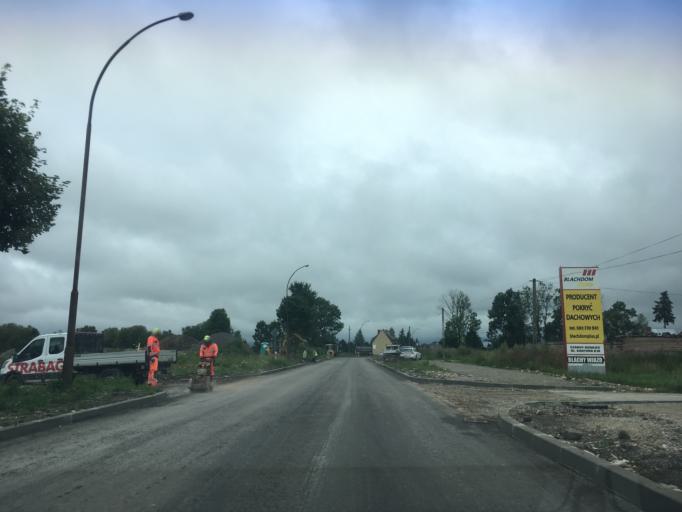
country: PL
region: Lesser Poland Voivodeship
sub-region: Powiat nowotarski
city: Czarny Dunajec
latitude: 49.4451
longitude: 19.8574
